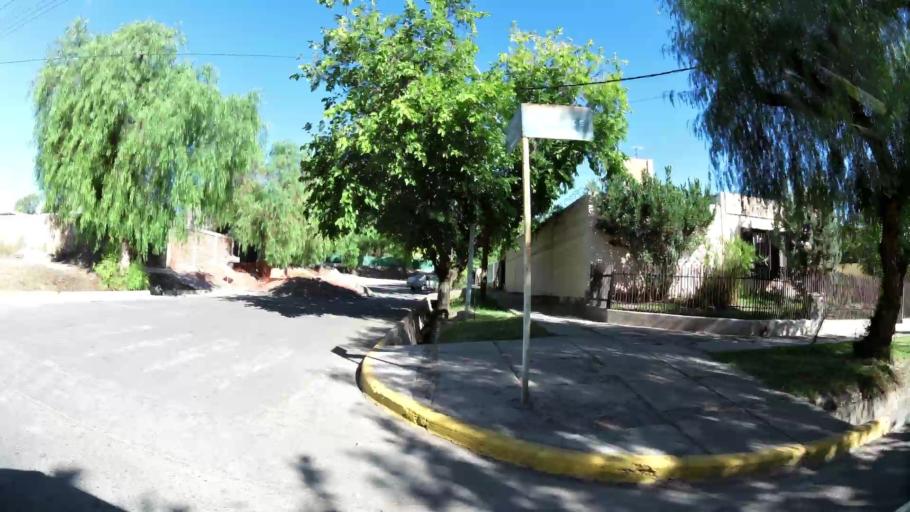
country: AR
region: Mendoza
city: Mendoza
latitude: -32.8777
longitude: -68.8733
